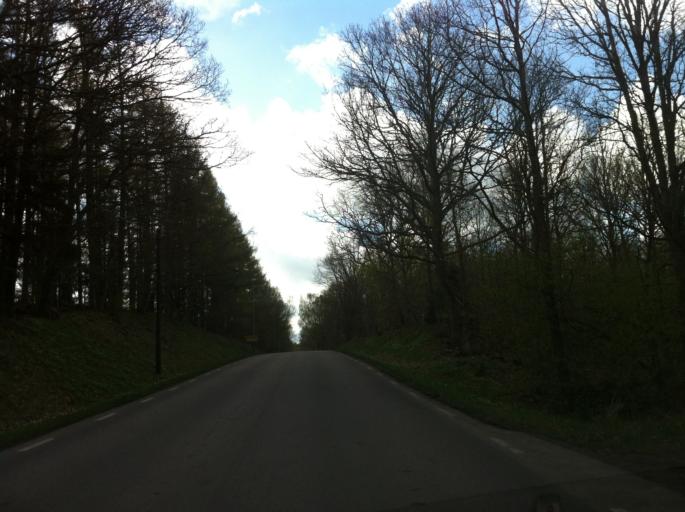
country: SE
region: Skane
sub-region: Horby Kommun
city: Hoerby
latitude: 55.8932
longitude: 13.6140
